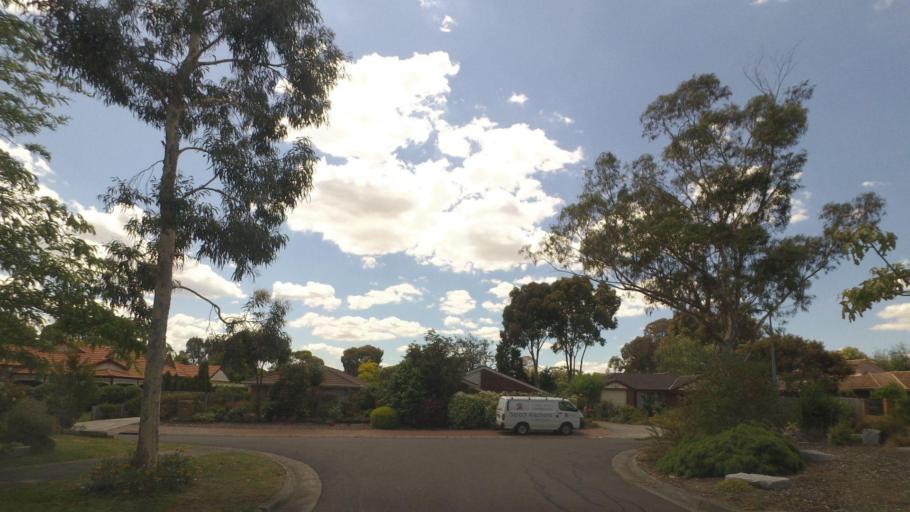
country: AU
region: Victoria
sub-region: Knox
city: Knoxfield
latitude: -37.8815
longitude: 145.2552
